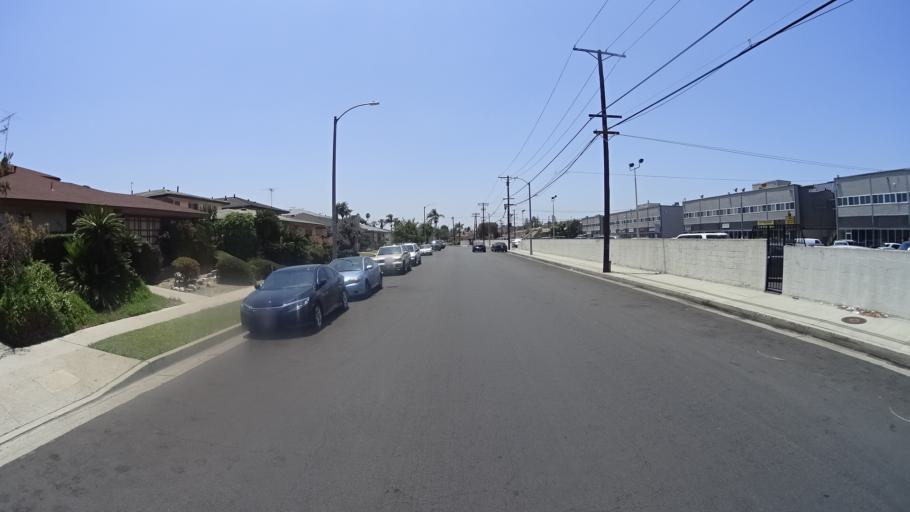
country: US
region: California
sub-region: Los Angeles County
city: View Park-Windsor Hills
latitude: 34.0161
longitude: -118.3340
